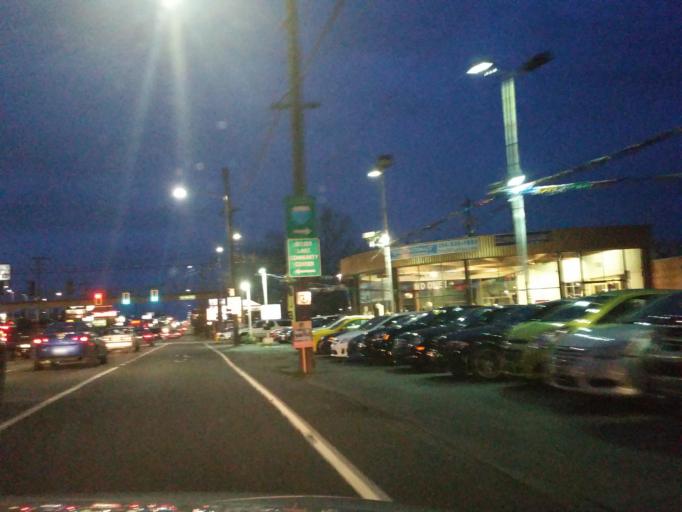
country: US
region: Washington
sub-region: King County
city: Shoreline
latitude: 47.7226
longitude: -122.3449
